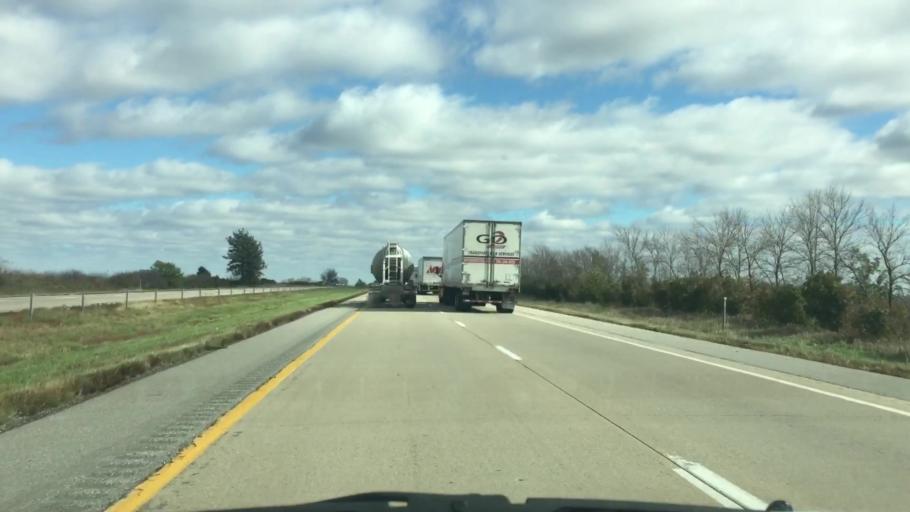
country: US
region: Iowa
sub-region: Poweshiek County
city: Brooklyn
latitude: 41.6961
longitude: -92.4194
